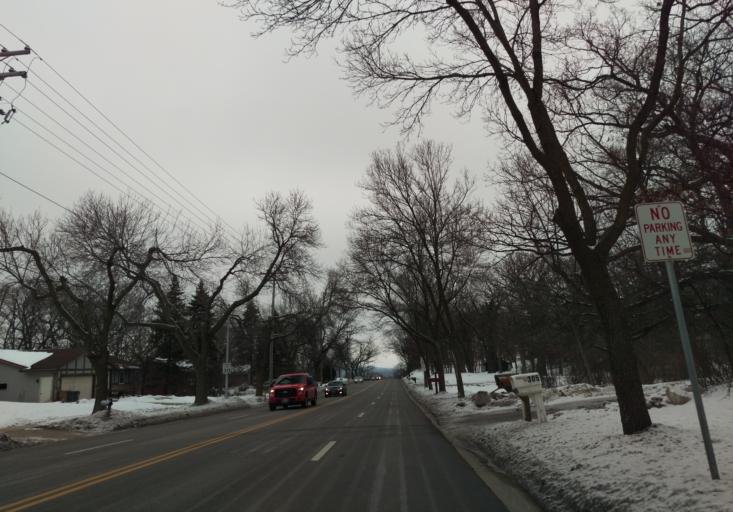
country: US
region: Wisconsin
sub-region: Dane County
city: Middleton
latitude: 43.0719
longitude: -89.5025
